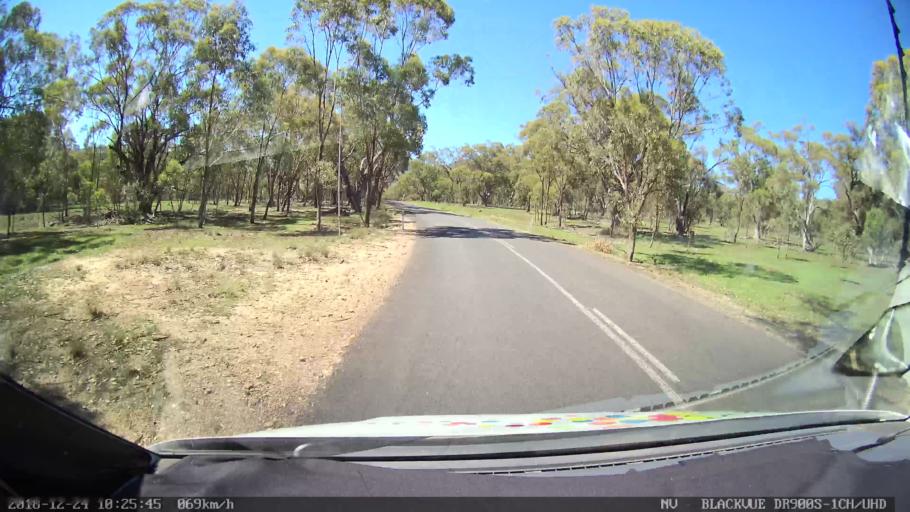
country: AU
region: New South Wales
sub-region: Liverpool Plains
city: Quirindi
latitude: -31.8023
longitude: 150.5274
